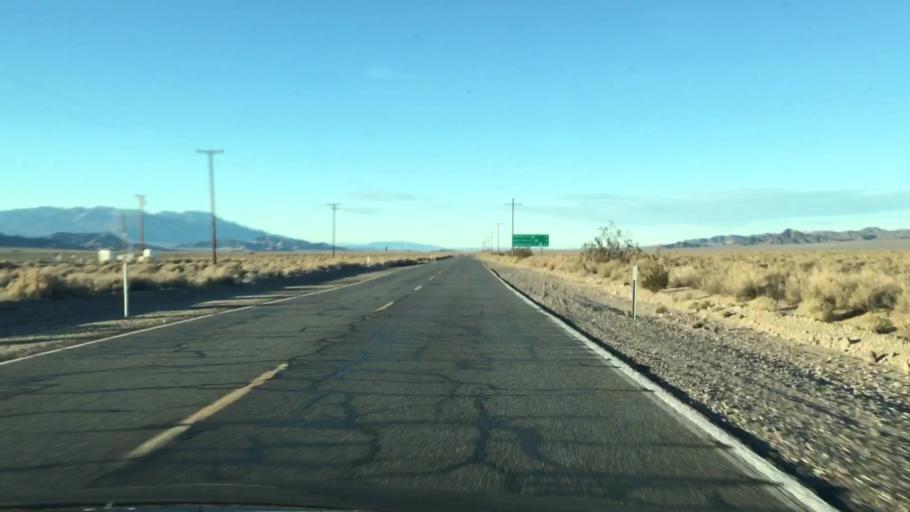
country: US
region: California
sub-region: San Bernardino County
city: Fort Irwin
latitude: 35.2862
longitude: -116.0791
